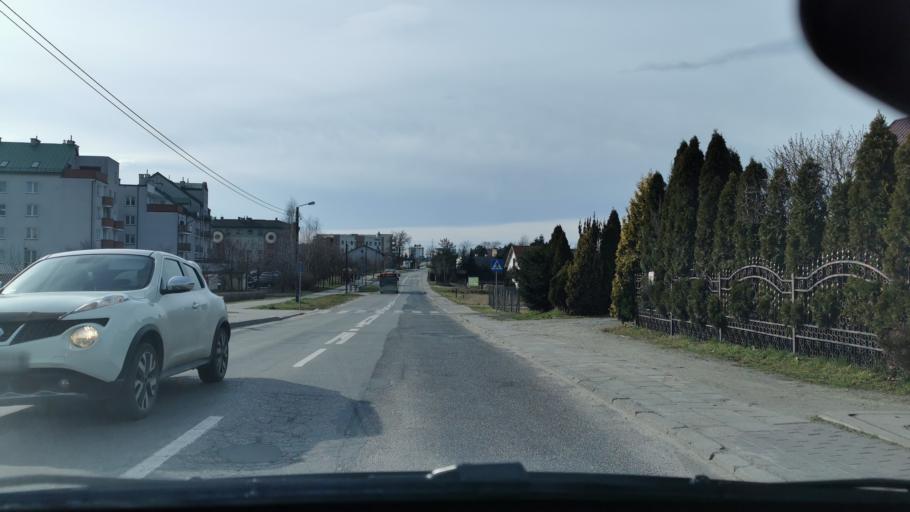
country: PL
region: Lublin Voivodeship
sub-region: Powiat lubelski
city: Lublin
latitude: 51.2022
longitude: 22.5430
